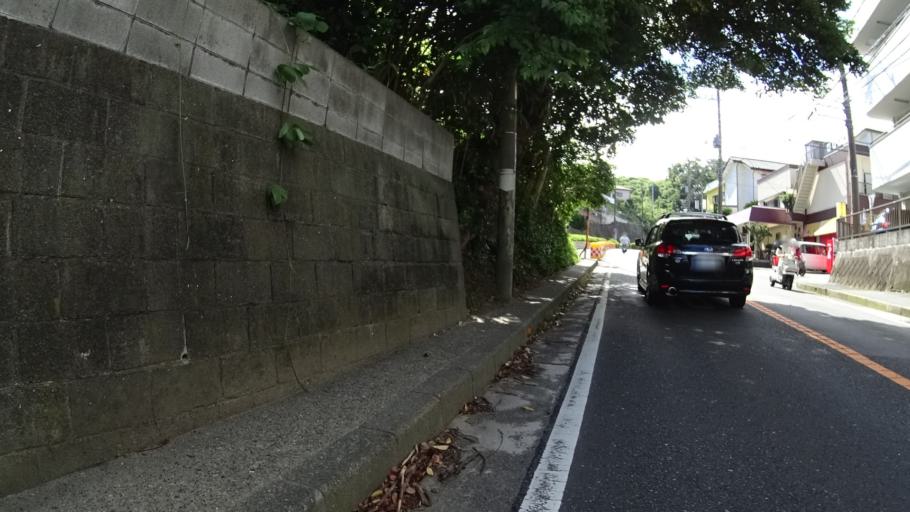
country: JP
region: Kanagawa
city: Yokosuka
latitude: 35.2586
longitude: 139.7068
